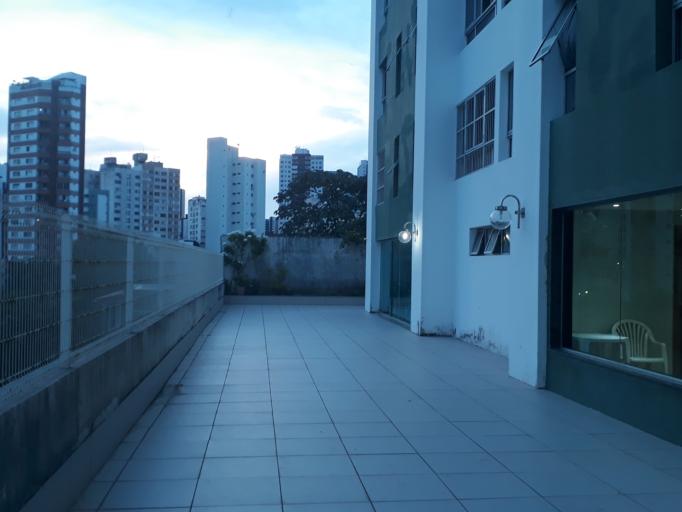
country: BR
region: Bahia
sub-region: Salvador
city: Salvador
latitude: -12.9927
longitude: -38.5173
